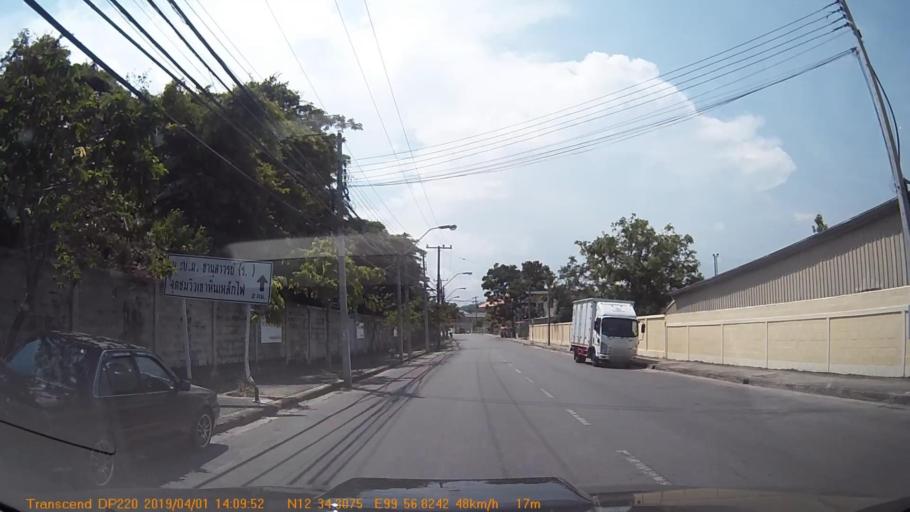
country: TH
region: Prachuap Khiri Khan
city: Hua Hin
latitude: 12.5720
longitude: 99.9467
